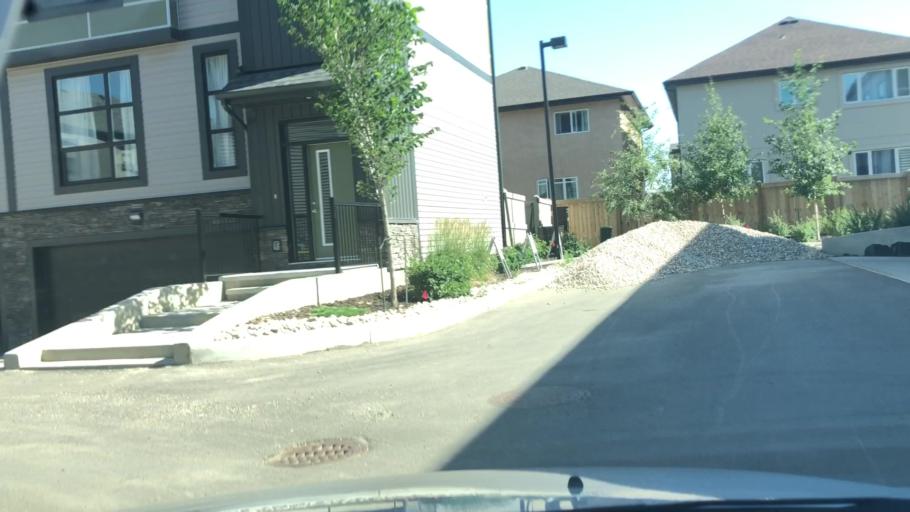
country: CA
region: Alberta
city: Edmonton
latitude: 53.6091
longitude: -113.5373
